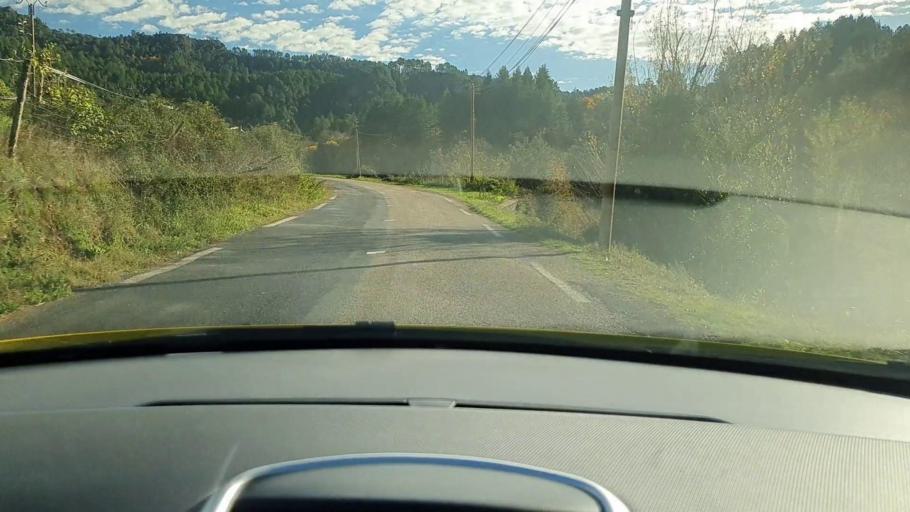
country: FR
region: Languedoc-Roussillon
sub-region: Departement du Gard
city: Valleraugue
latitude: 44.1259
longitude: 3.7561
